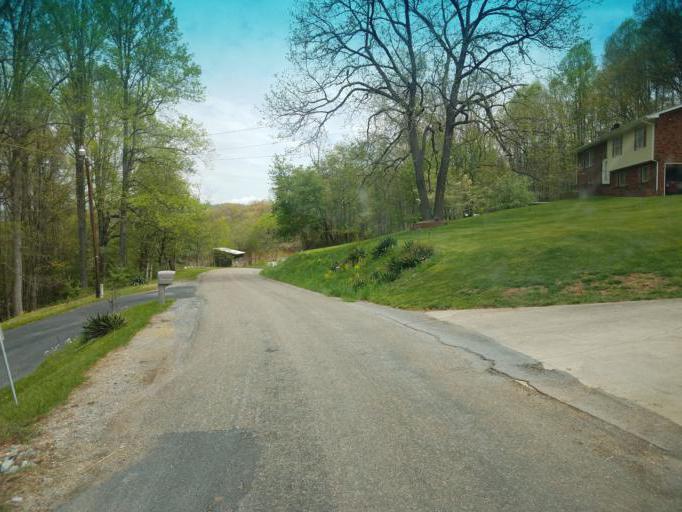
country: US
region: Virginia
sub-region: Smyth County
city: Marion
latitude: 36.7995
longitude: -81.4631
